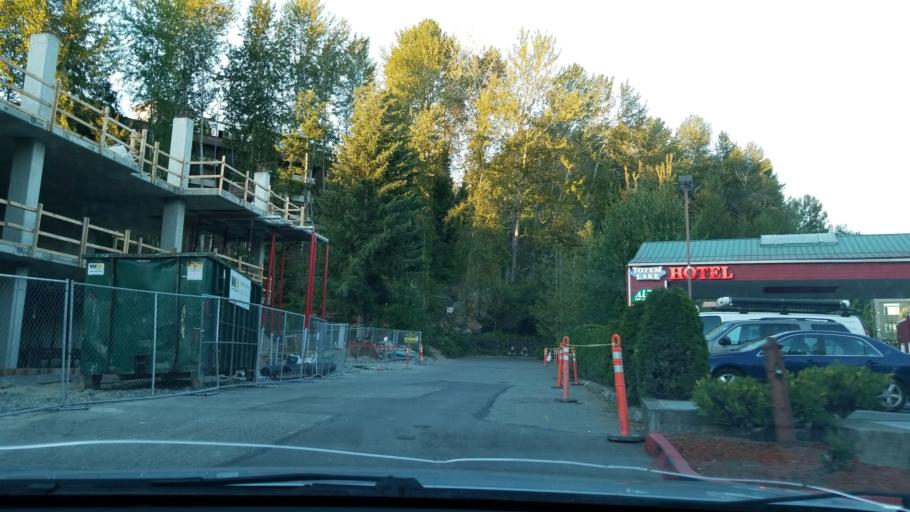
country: US
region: Washington
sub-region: King County
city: Kingsgate
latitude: 47.7123
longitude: -122.1773
